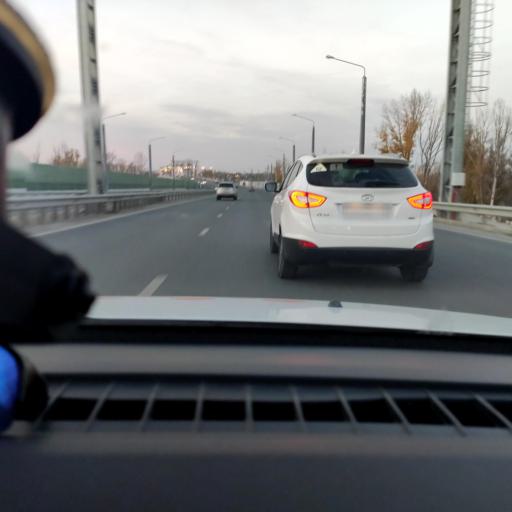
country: RU
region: Samara
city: Samara
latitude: 53.1679
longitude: 50.0855
